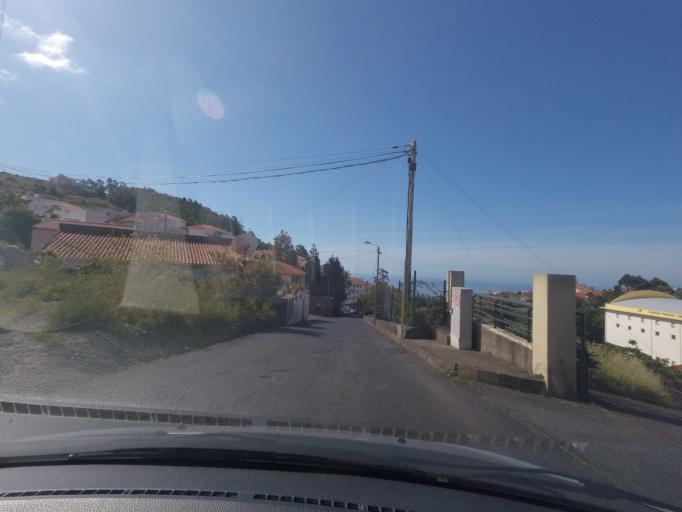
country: PT
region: Madeira
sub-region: Santa Cruz
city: Camacha
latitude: 32.6574
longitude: -16.8555
